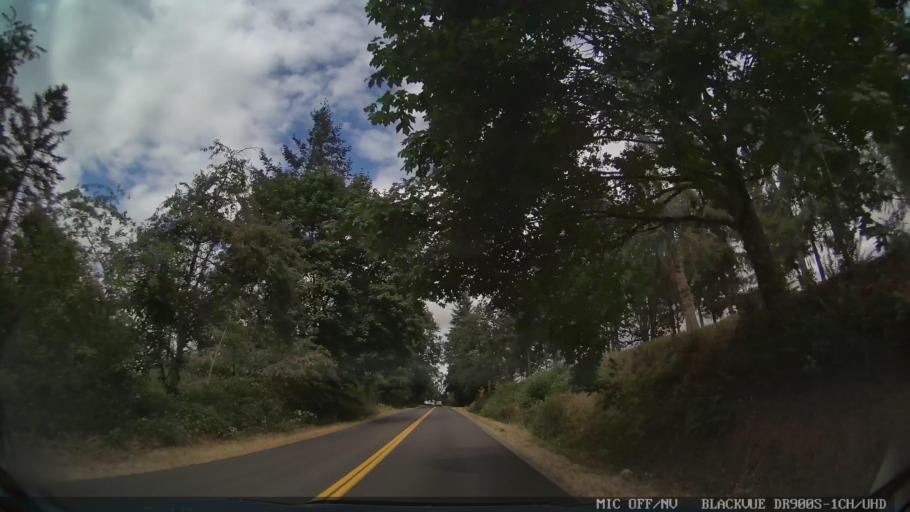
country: US
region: Oregon
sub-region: Marion County
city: Aumsville
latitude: 44.8635
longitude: -122.8501
